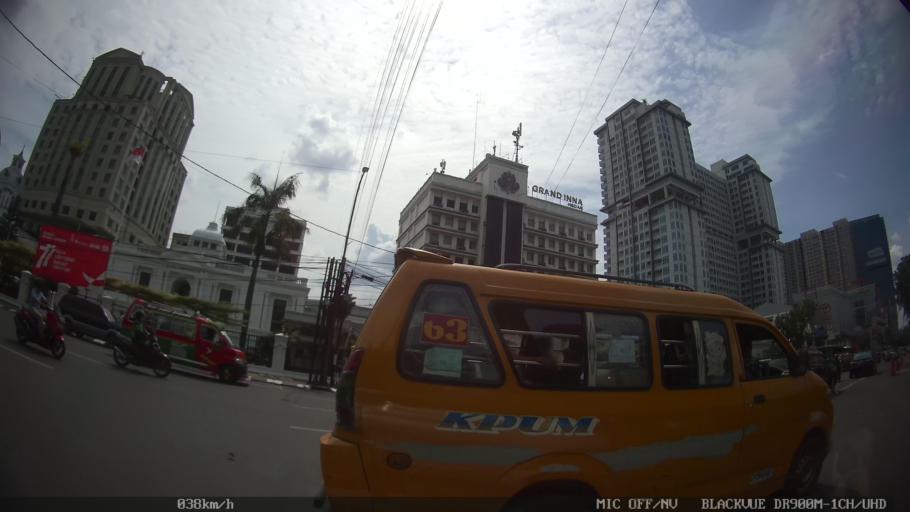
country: ID
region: North Sumatra
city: Medan
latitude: 3.5909
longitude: 98.6776
